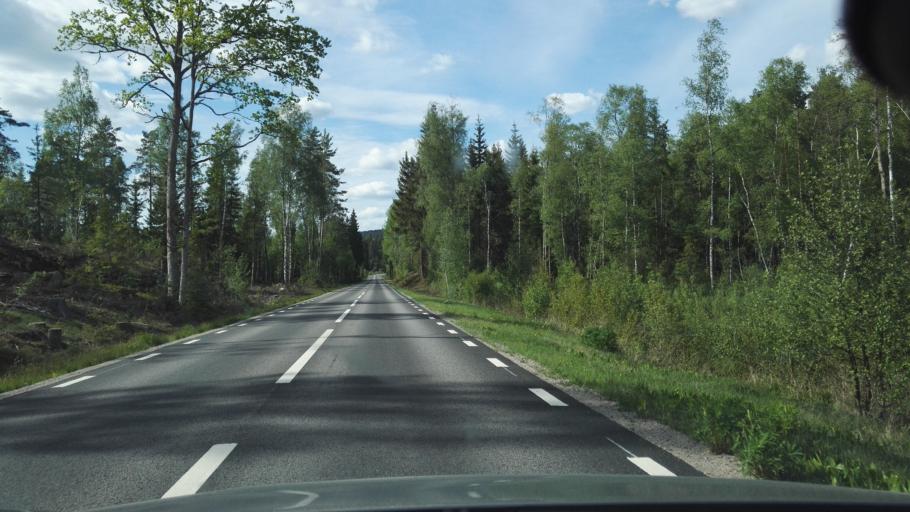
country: SE
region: Kronoberg
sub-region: Vaxjo Kommun
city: Braas
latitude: 57.1410
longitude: 14.9632
